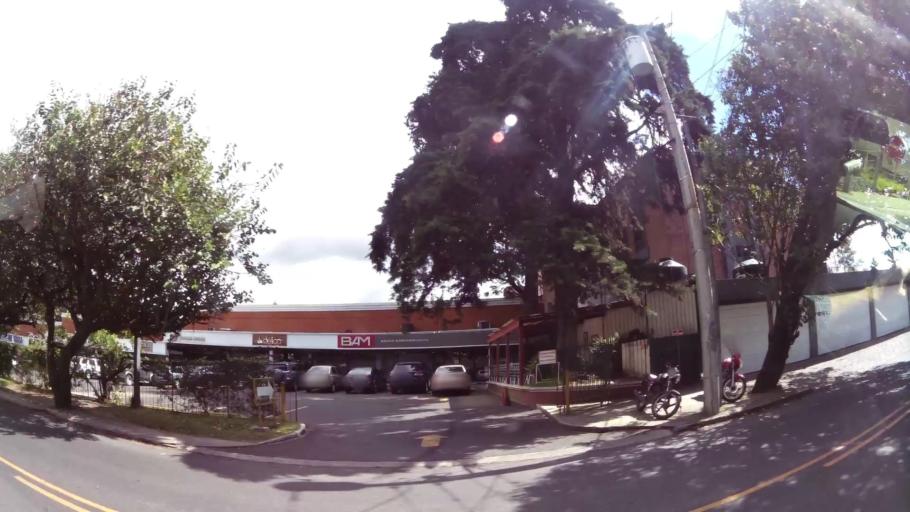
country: GT
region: Guatemala
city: Santa Catarina Pinula
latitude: 14.5825
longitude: -90.5148
